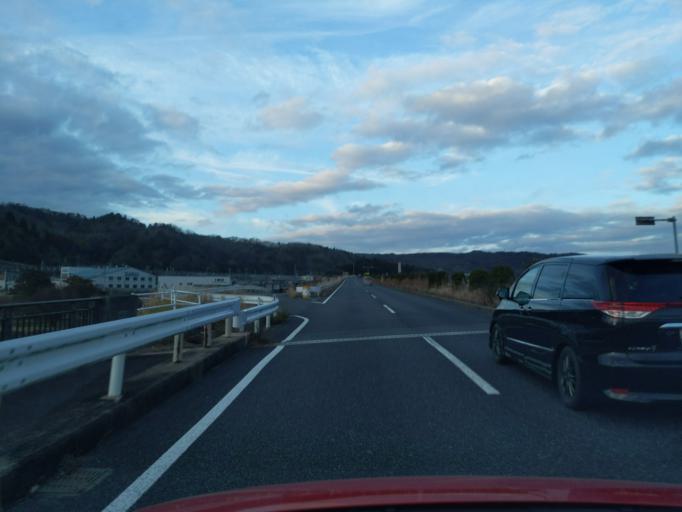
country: JP
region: Gifu
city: Mizunami
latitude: 35.3860
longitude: 137.2708
